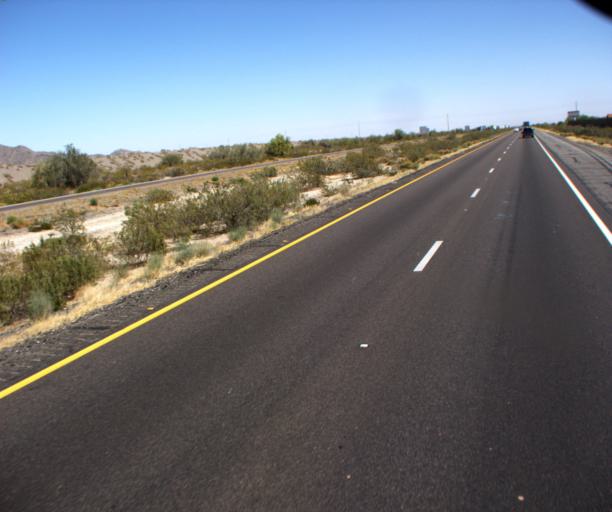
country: US
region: Arizona
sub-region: Maricopa County
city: Buckeye
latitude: 33.4483
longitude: -112.5448
